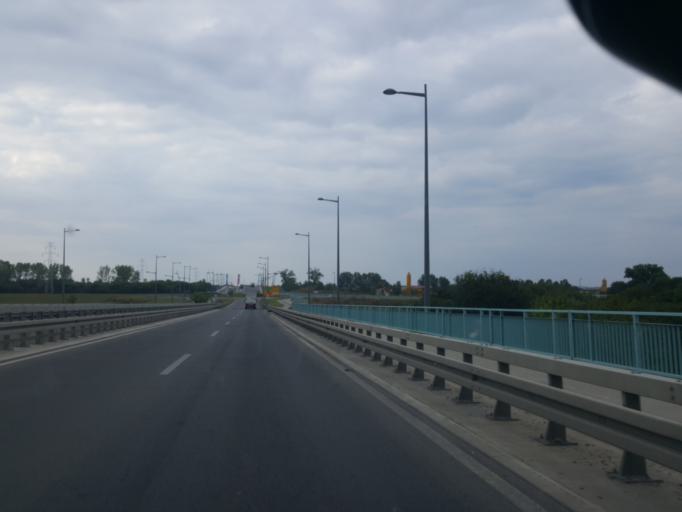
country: RS
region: Autonomna Pokrajina Vojvodina
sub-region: Juznobacki Okrug
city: Novi Sad
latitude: 45.2794
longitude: 19.8026
